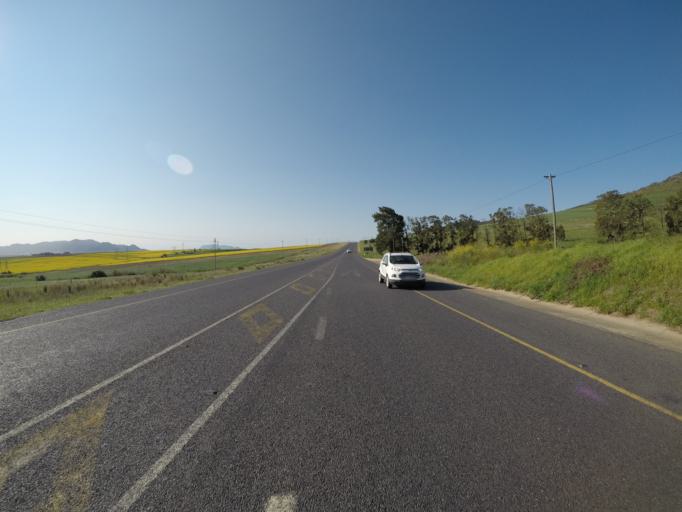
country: ZA
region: Western Cape
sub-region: Cape Winelands District Municipality
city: Noorder-Paarl
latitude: -33.7061
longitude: 18.8936
